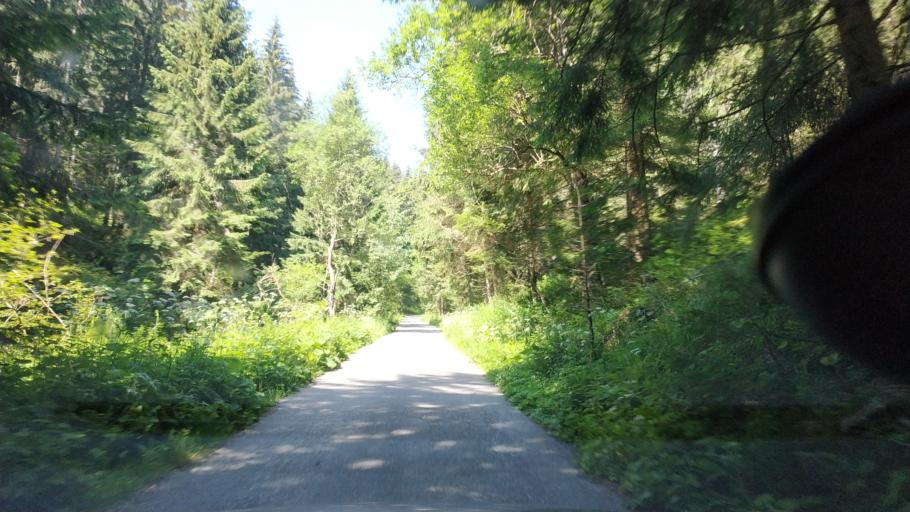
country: SK
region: Zilinsky
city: Ruzomberok
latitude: 48.9970
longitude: 19.2309
